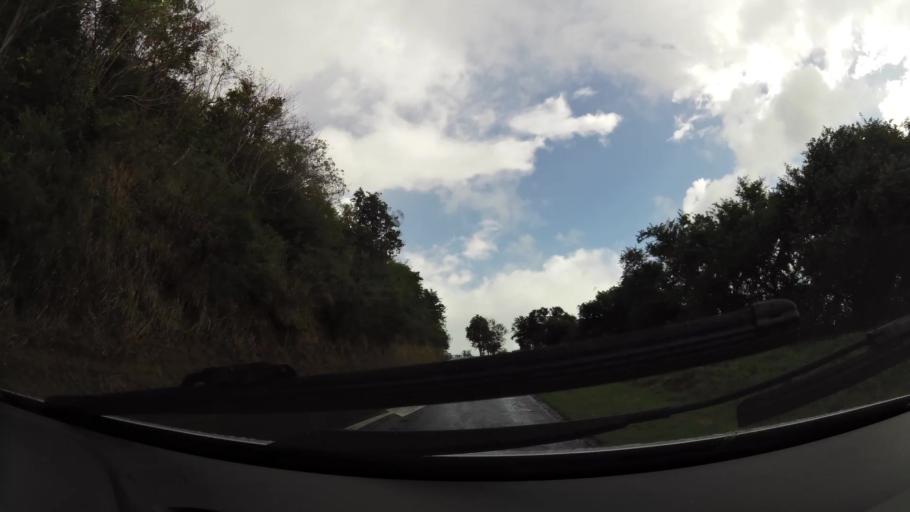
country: MQ
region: Martinique
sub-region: Martinique
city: Les Trois-Ilets
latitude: 14.5423
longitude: -61.0477
